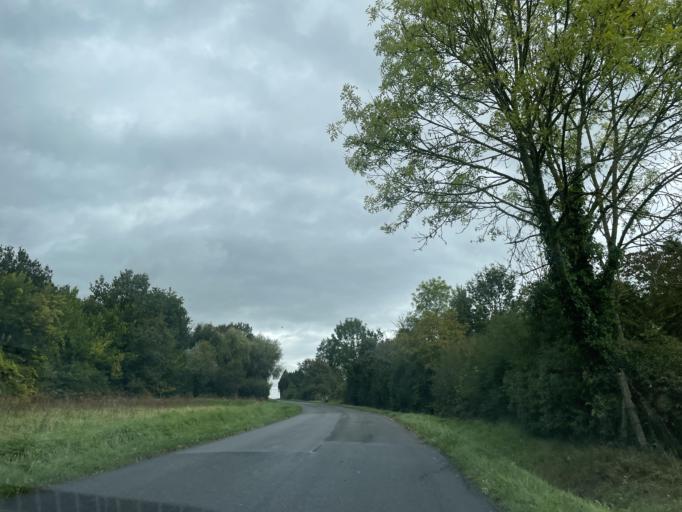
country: FR
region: Ile-de-France
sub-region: Departement de Seine-et-Marne
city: Coulommiers
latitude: 48.8167
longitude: 3.1058
